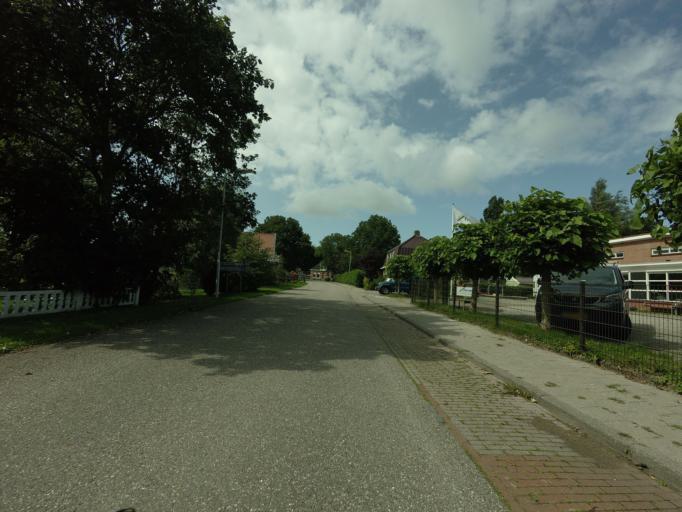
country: NL
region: Friesland
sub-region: Sudwest Fryslan
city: Makkum
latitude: 53.0848
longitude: 5.4256
